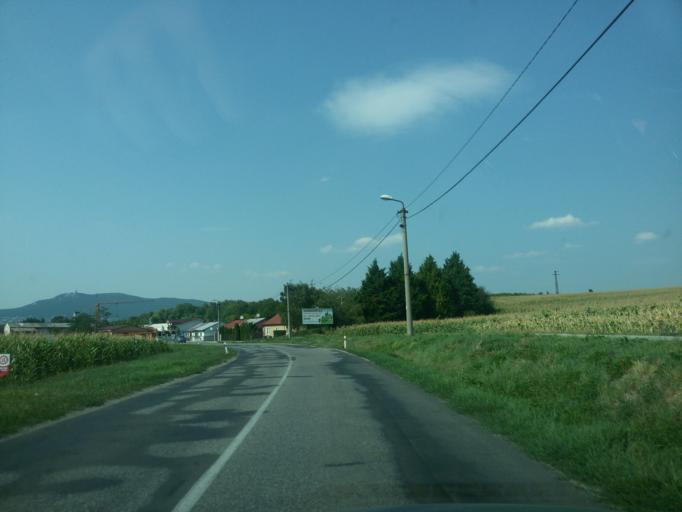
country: SK
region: Nitriansky
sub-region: Okres Nitra
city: Nitra
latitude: 48.2943
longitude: 18.1282
